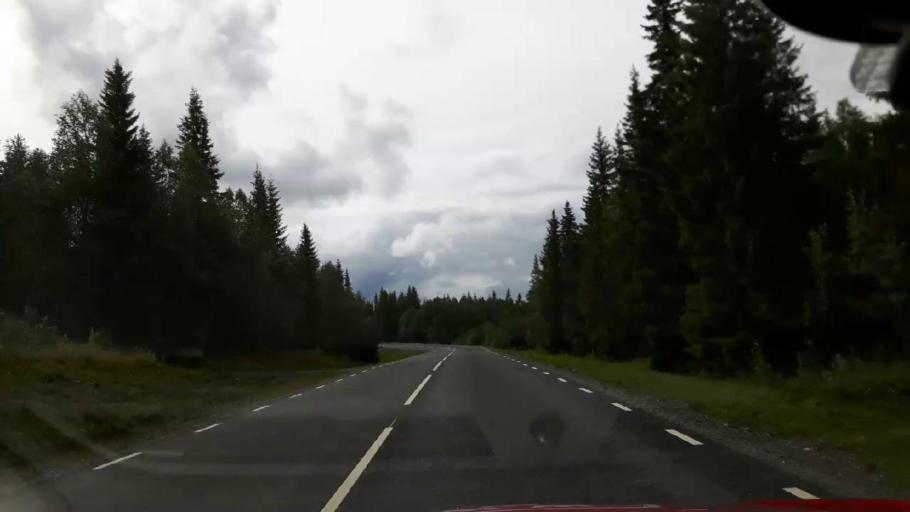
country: NO
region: Nord-Trondelag
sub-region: Lierne
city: Sandvika
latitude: 64.6409
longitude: 14.1381
